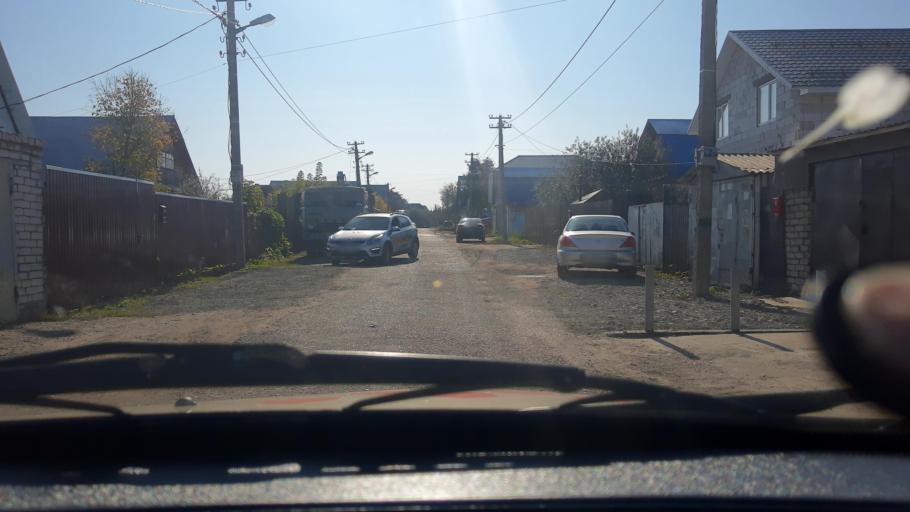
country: RU
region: Bashkortostan
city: Ufa
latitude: 54.7449
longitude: 55.9081
